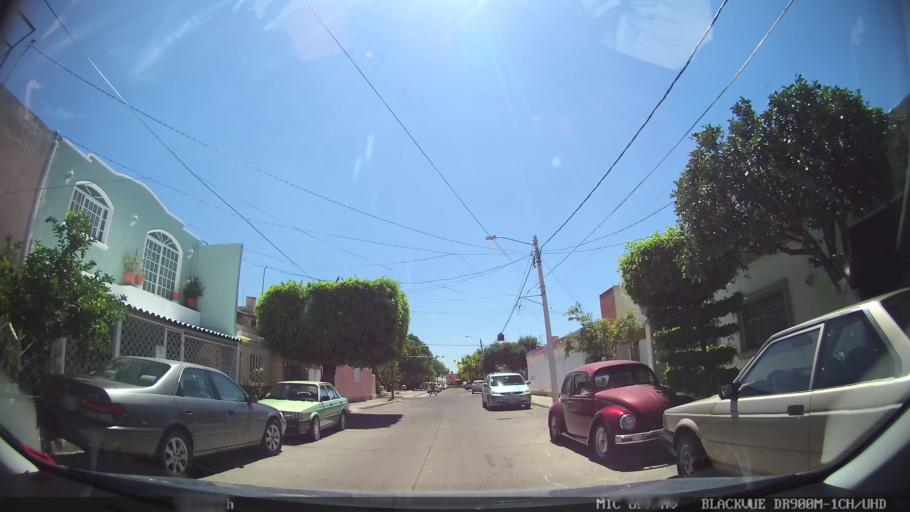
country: MX
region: Jalisco
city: Tlaquepaque
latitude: 20.6696
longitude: -103.2911
